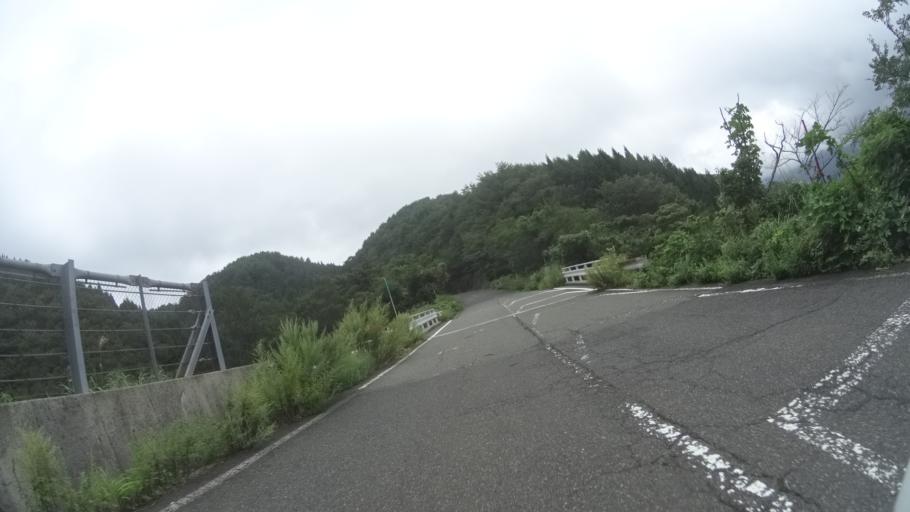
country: JP
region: Tottori
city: Kurayoshi
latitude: 35.4014
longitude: 134.0027
